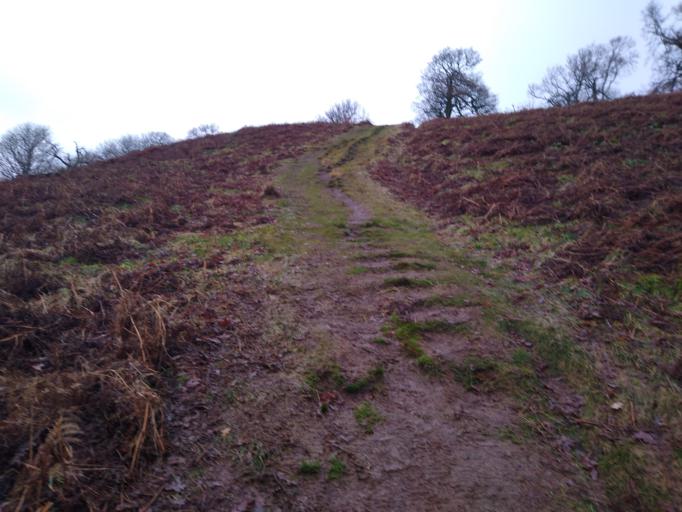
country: GB
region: England
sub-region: Cumbria
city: Penrith
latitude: 54.6127
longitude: -2.9257
